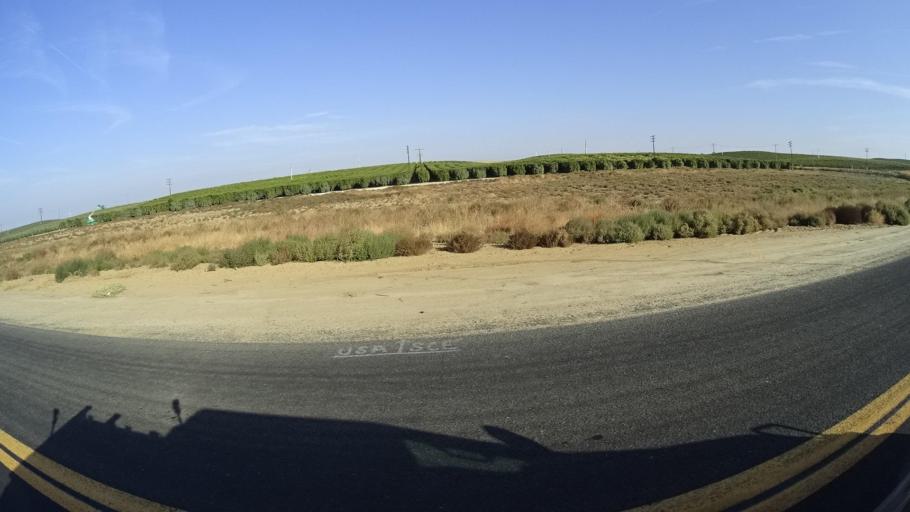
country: US
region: California
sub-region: Tulare County
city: Richgrove
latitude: 35.6588
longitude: -119.0789
